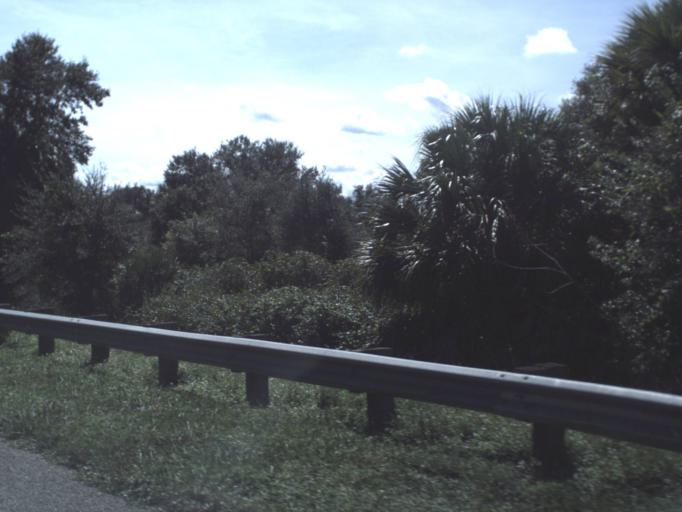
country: US
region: Florida
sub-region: Glades County
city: Moore Haven
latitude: 26.8928
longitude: -81.2372
